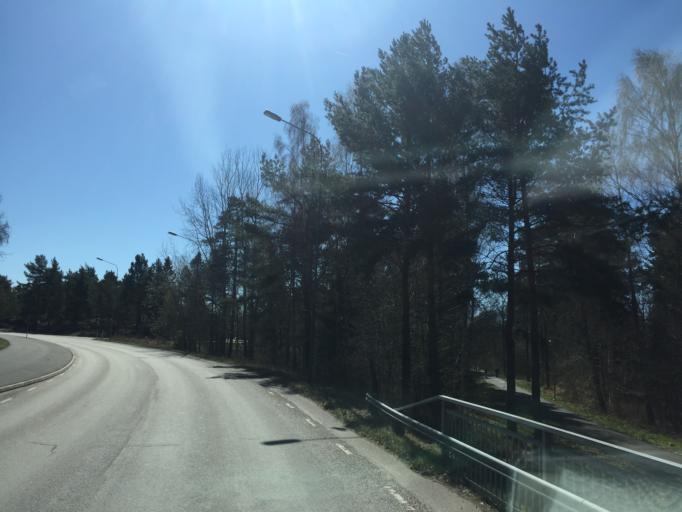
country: SE
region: Kalmar
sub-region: Oskarshamns Kommun
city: Oskarshamn
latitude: 57.2483
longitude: 16.4606
